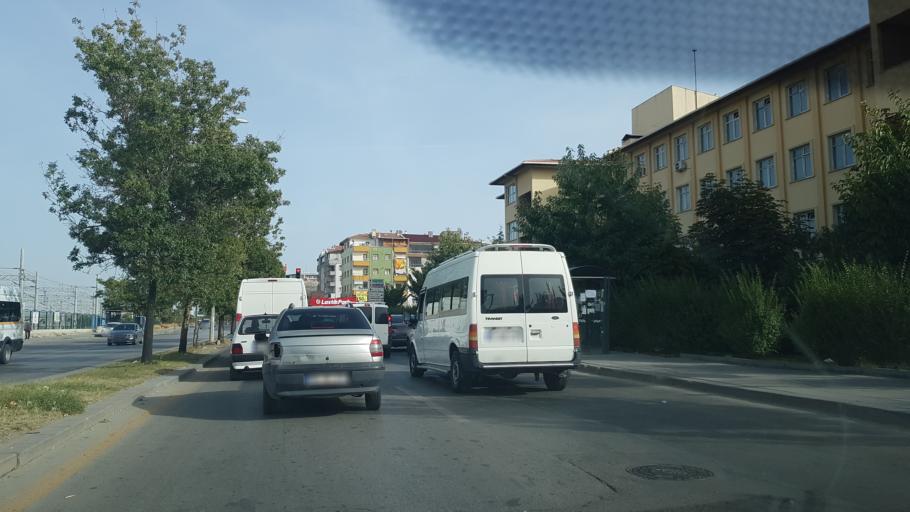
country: TR
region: Ankara
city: Etimesgut
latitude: 39.9575
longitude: 32.6143
